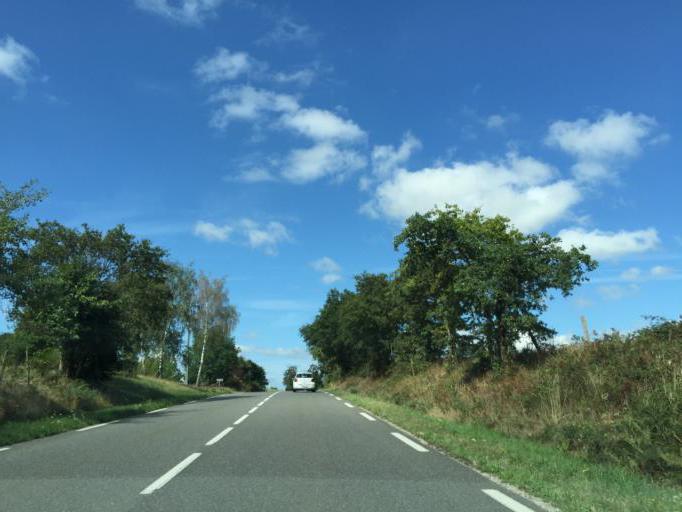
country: FR
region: Midi-Pyrenees
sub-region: Departement de l'Aveyron
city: Rieupeyroux
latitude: 44.3060
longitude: 2.1566
